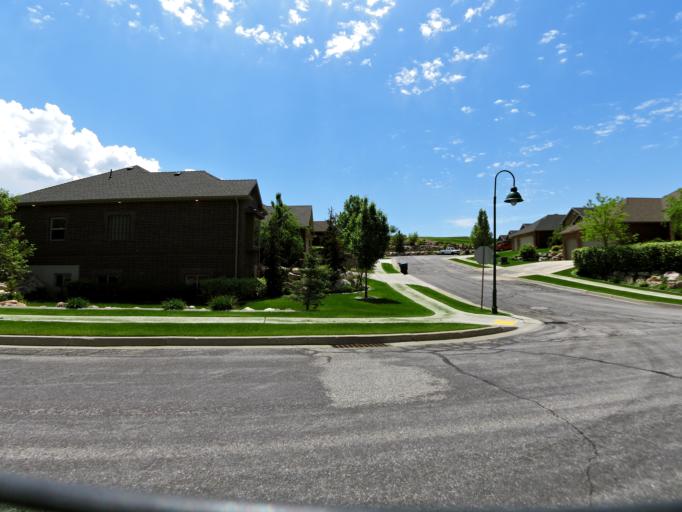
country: US
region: Utah
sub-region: Weber County
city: Uintah
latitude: 41.1631
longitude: -111.9270
